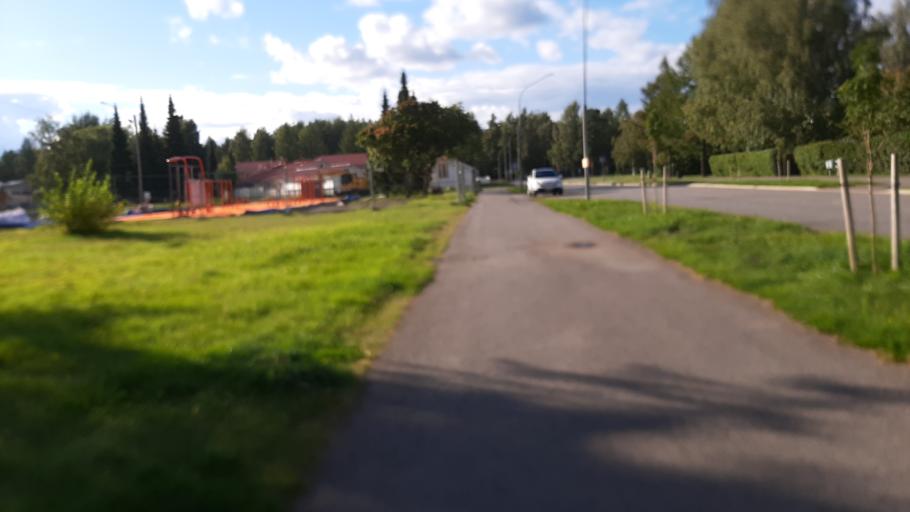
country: FI
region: North Karelia
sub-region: Joensuu
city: Joensuu
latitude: 62.6131
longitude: 29.7910
